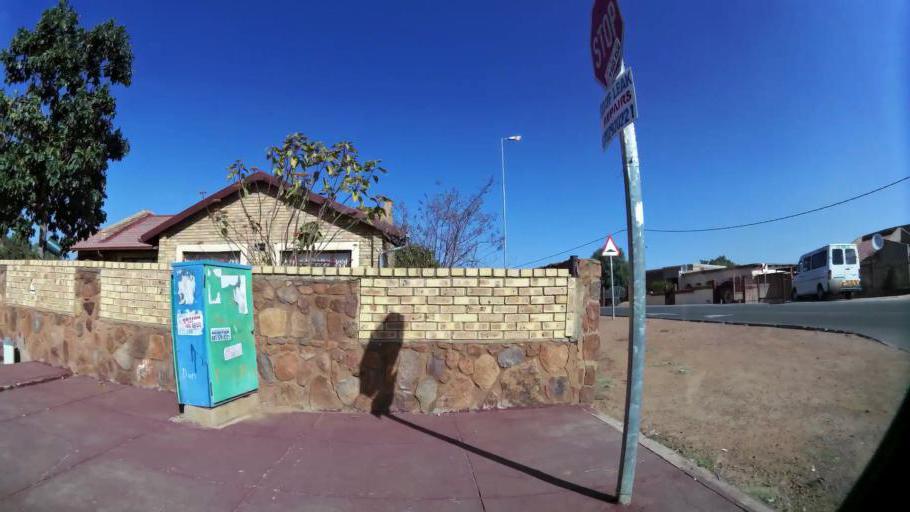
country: ZA
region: Gauteng
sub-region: City of Tshwane Metropolitan Municipality
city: Mabopane
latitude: -25.5326
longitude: 28.0887
